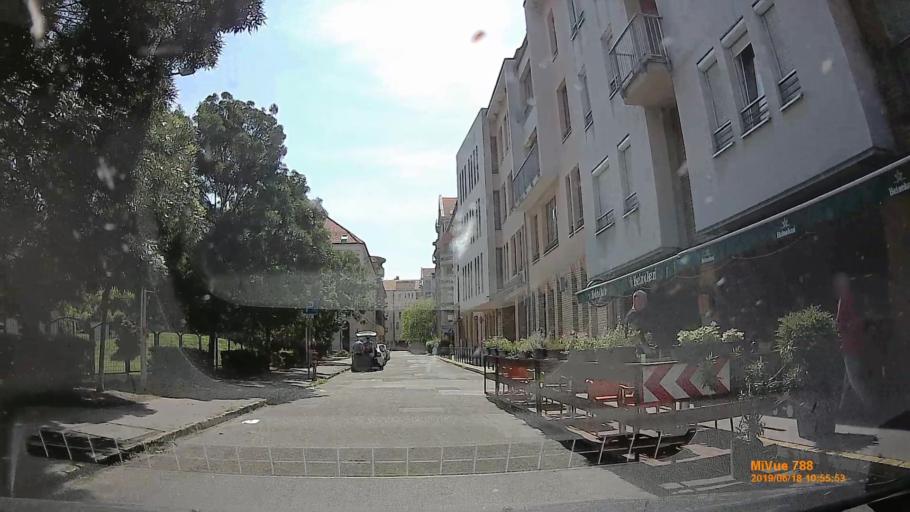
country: HU
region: Budapest
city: Budapest VIII. keruelet
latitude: 47.4794
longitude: 19.0795
